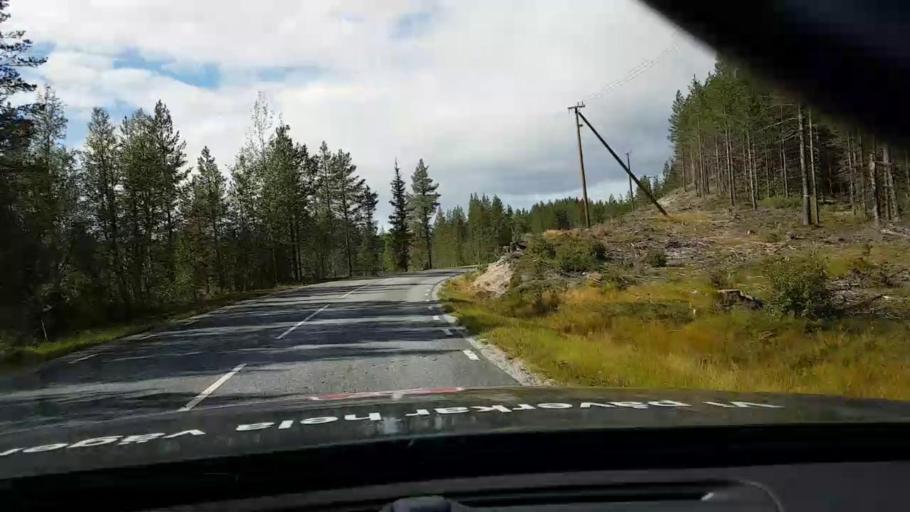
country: SE
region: Vaesterbotten
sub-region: Asele Kommun
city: Asele
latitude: 63.8483
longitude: 17.4053
